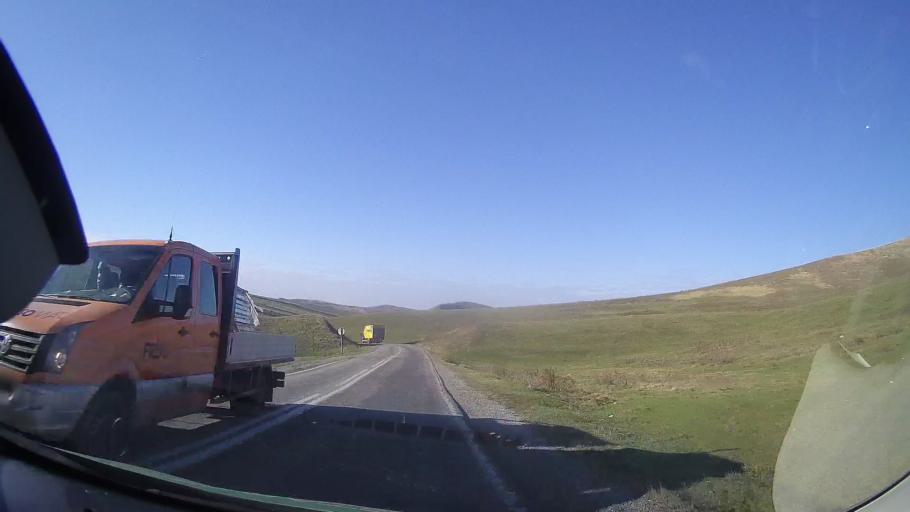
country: RO
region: Mures
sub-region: Comuna Sarmasu
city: Sarmasu
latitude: 46.7956
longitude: 24.1800
